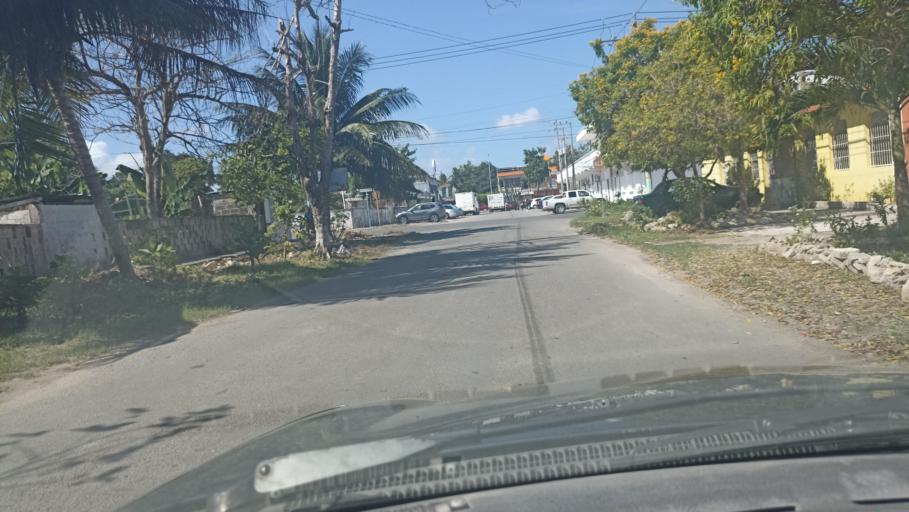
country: MX
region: Quintana Roo
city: Chetumal
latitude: 18.5110
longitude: -88.2895
